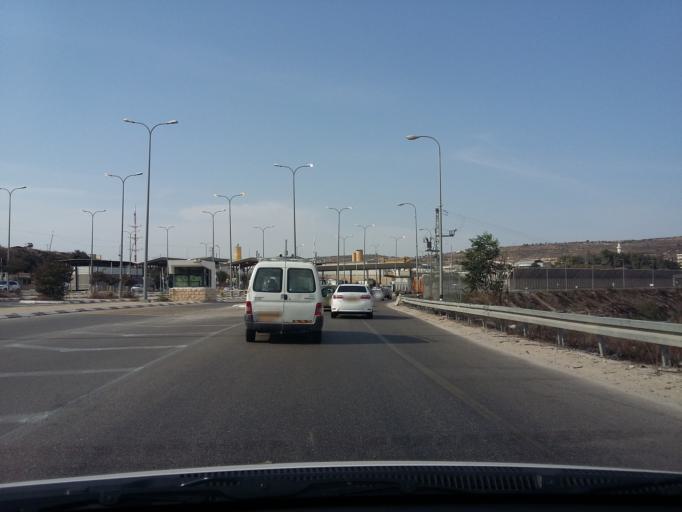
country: PS
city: Ad Dawhah
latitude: 31.7066
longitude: 35.1701
